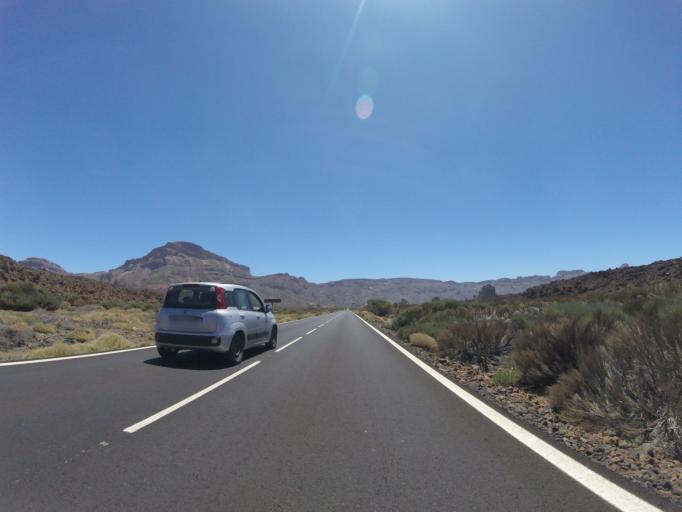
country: ES
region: Canary Islands
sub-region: Provincia de Santa Cruz de Tenerife
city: Vilaflor
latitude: 28.2383
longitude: -16.6300
